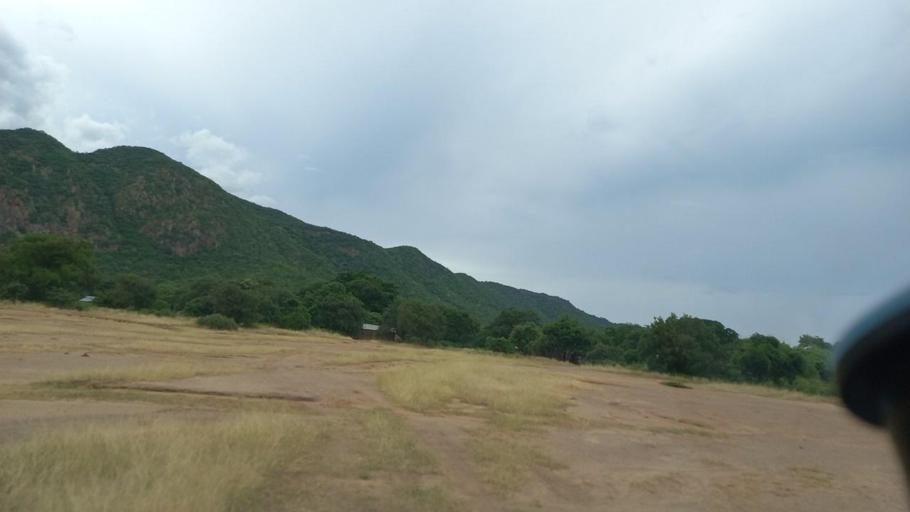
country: ZM
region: Lusaka
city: Luangwa
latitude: -15.6177
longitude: 30.2652
